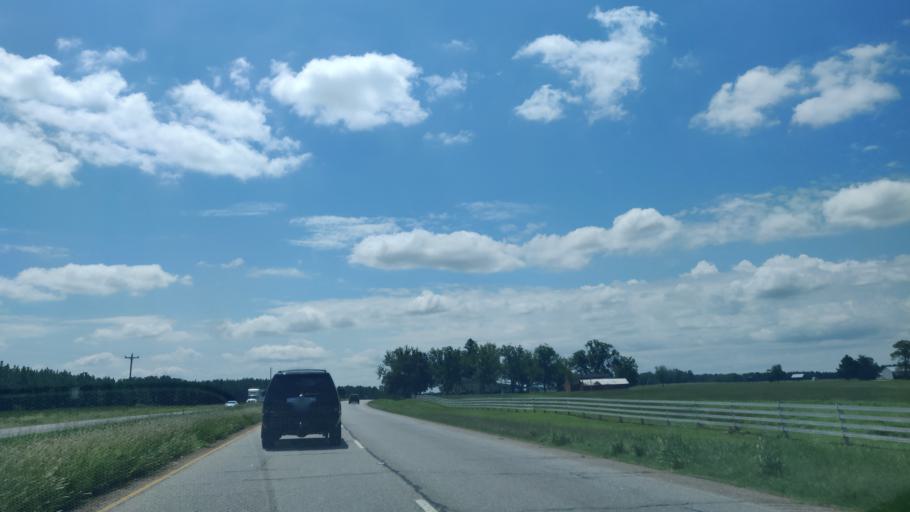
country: US
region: Georgia
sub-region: Stewart County
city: Richland
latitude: 32.0231
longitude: -84.6669
